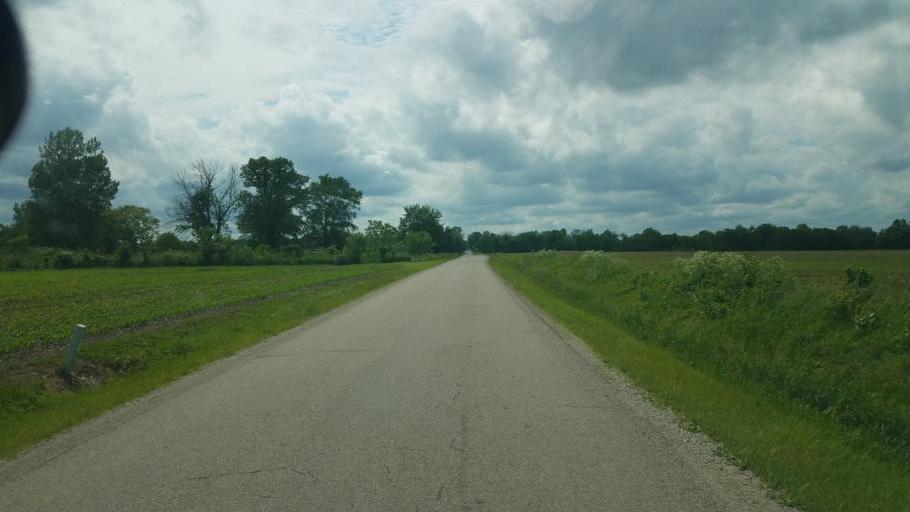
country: US
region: Ohio
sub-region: Fairfield County
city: Millersport
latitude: 39.9370
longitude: -82.5740
